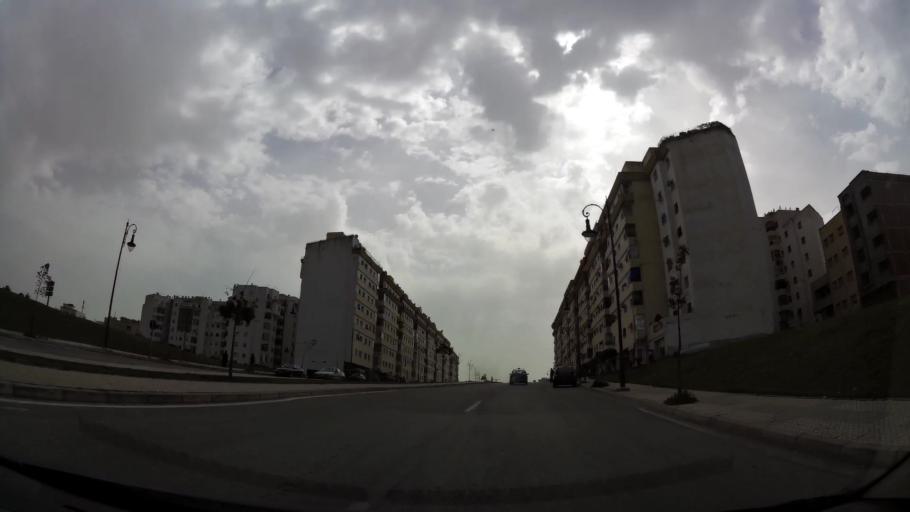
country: MA
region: Tanger-Tetouan
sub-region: Tanger-Assilah
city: Tangier
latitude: 35.7506
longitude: -5.8460
